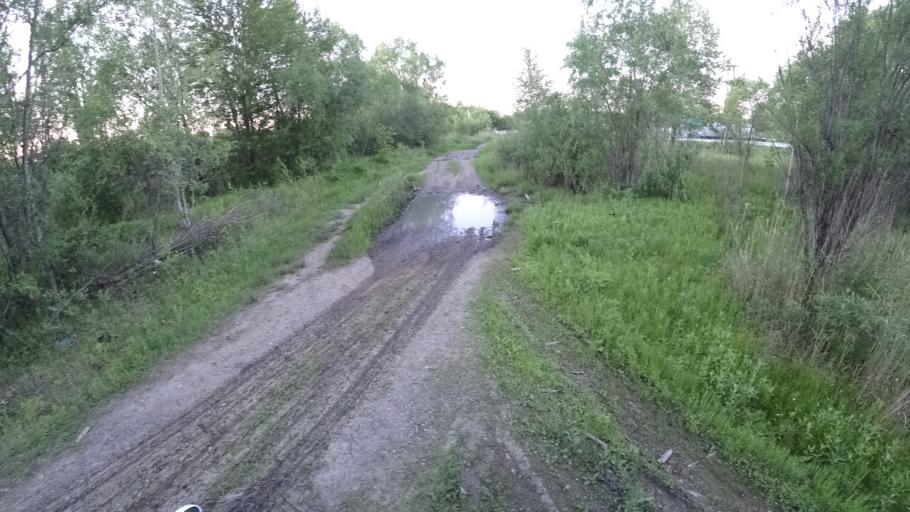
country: RU
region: Khabarovsk Krai
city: Khor
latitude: 47.8500
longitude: 134.9540
